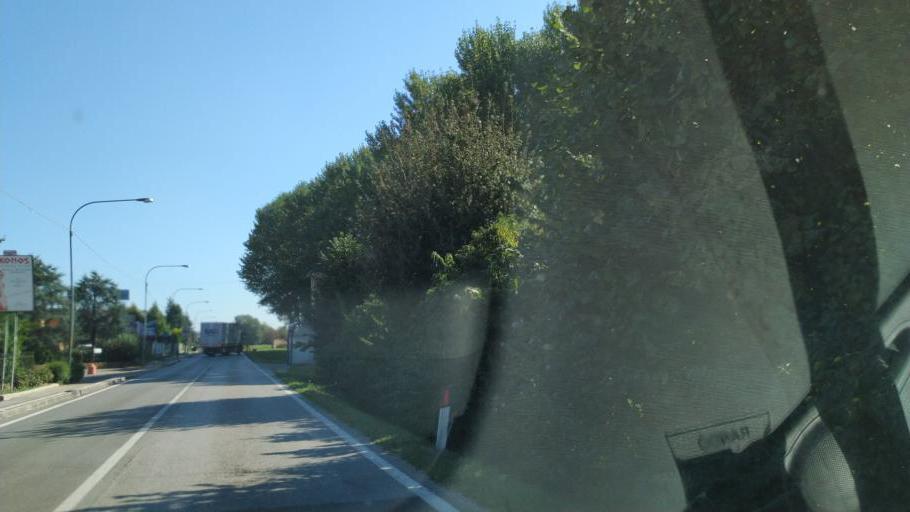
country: IT
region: Emilia-Romagna
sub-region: Provincia di Ferrara
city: Mirabello
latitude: 44.8170
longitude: 11.4473
